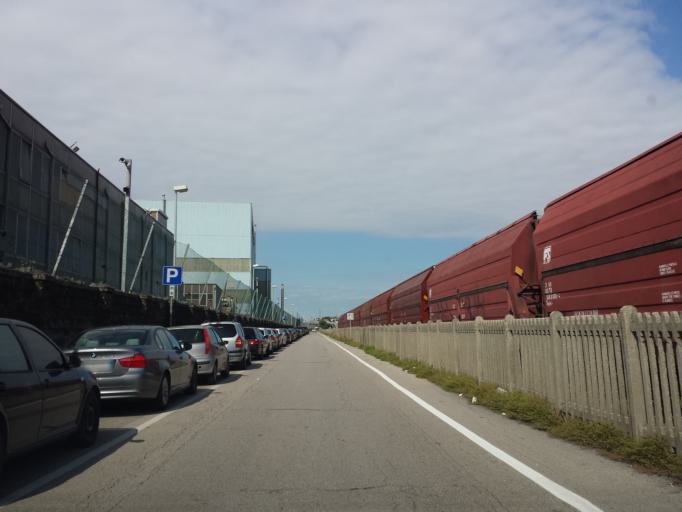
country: IT
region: Veneto
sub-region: Provincia di Venezia
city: Mestre
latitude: 45.4769
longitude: 12.2475
